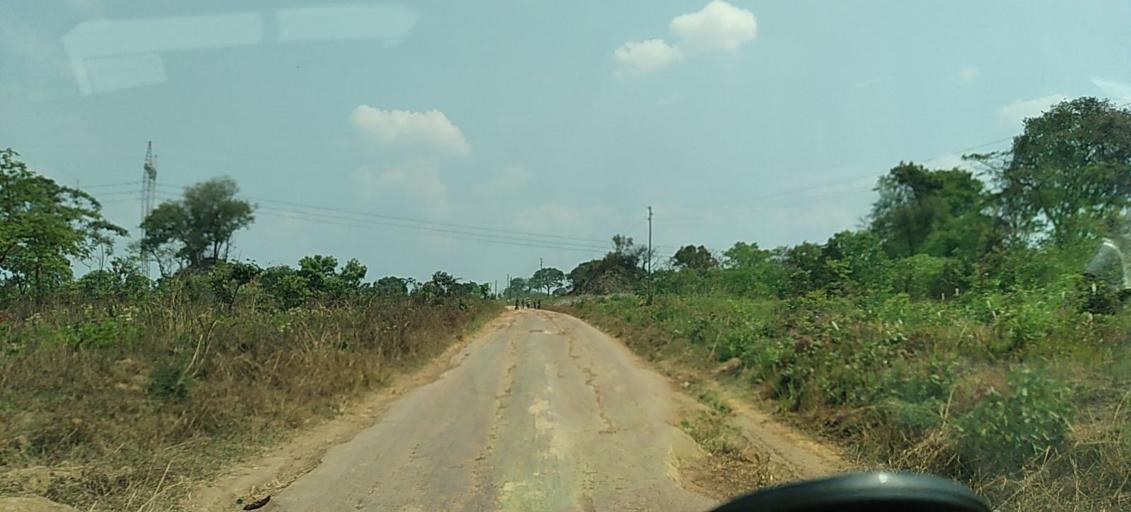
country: ZM
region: North-Western
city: Solwezi
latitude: -12.1153
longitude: 26.3674
